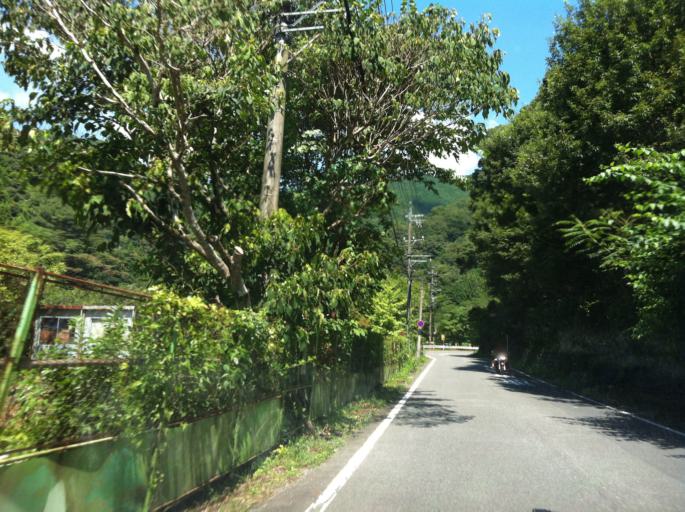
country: JP
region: Shizuoka
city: Shizuoka-shi
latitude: 35.0367
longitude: 138.2583
